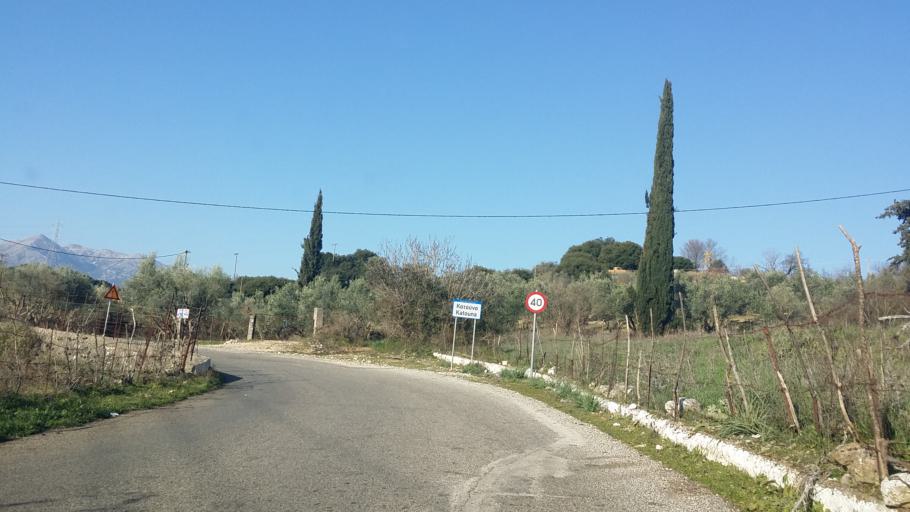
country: GR
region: West Greece
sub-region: Nomos Aitolias kai Akarnanias
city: Katouna
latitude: 38.7807
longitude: 21.1188
